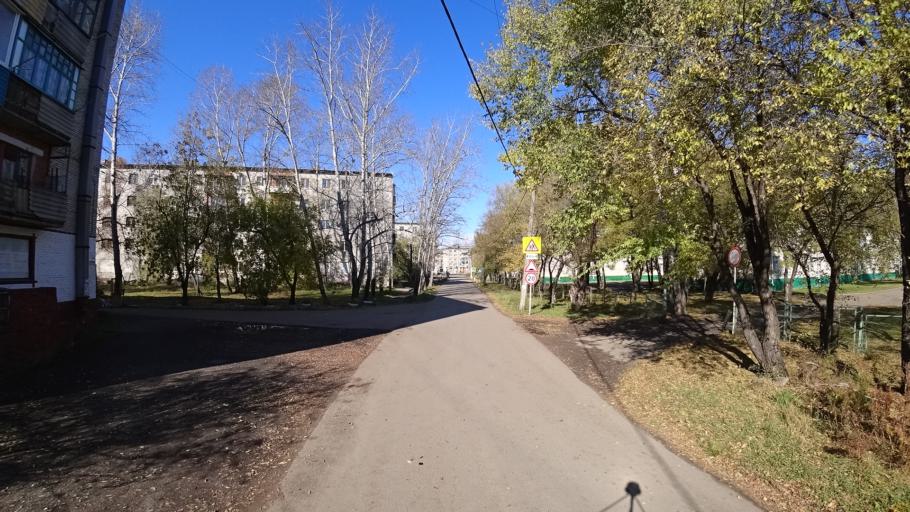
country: RU
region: Khabarovsk Krai
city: Amursk
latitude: 50.0976
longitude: 136.5146
